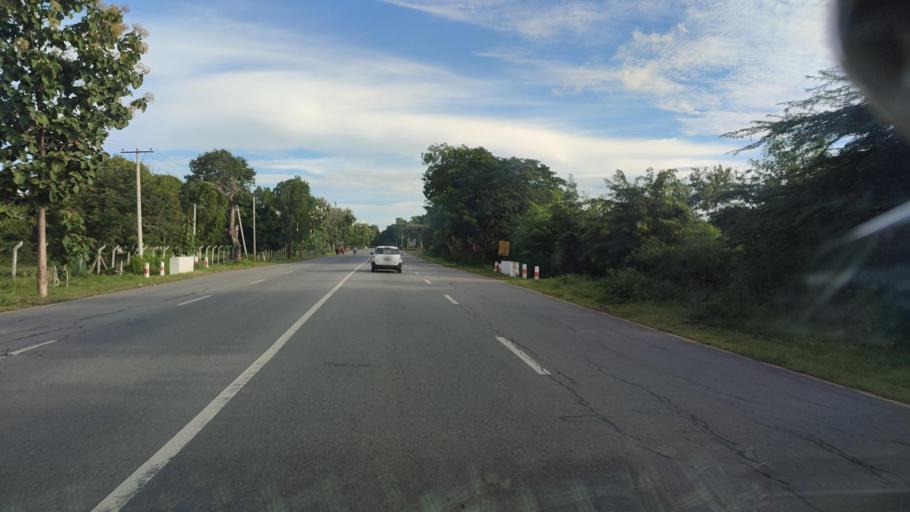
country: MM
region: Mandalay
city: Yamethin
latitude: 20.1549
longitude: 96.1917
